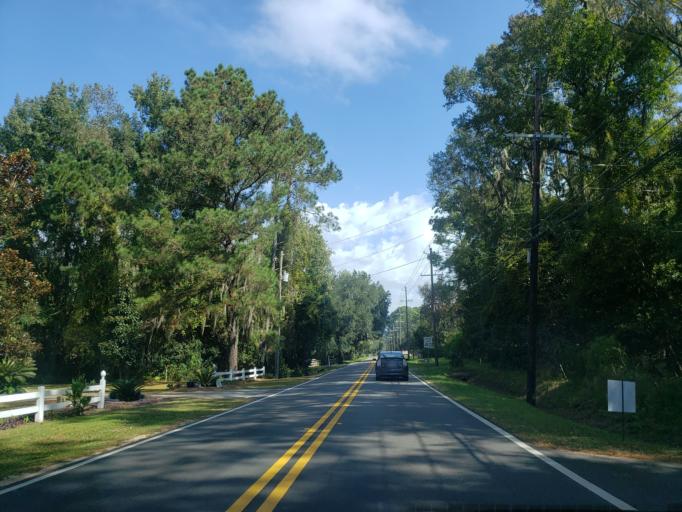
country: US
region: Georgia
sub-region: Chatham County
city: Montgomery
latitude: 31.9510
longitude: -81.1051
